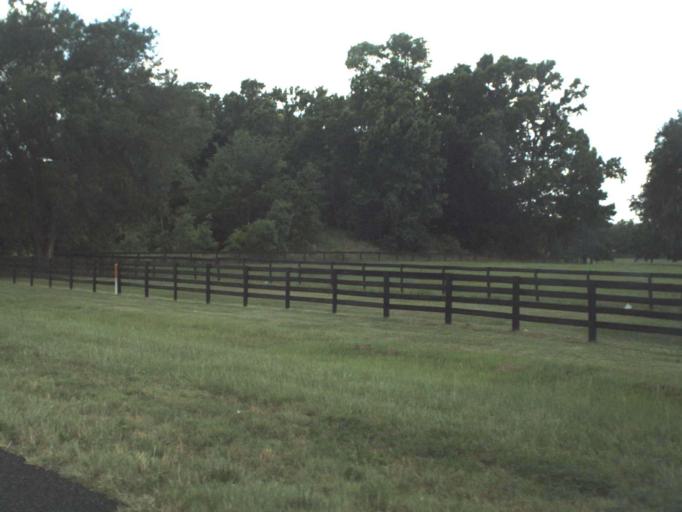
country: US
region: Florida
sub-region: Marion County
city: Citra
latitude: 29.3093
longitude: -82.1519
